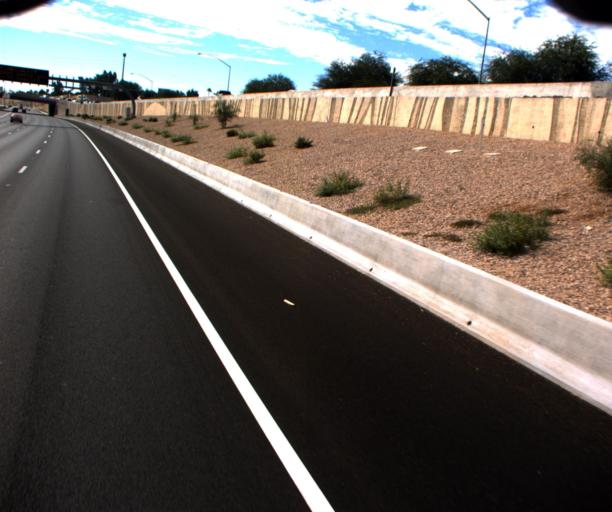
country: US
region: Arizona
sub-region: Maricopa County
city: Paradise Valley
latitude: 33.5851
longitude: -111.8918
